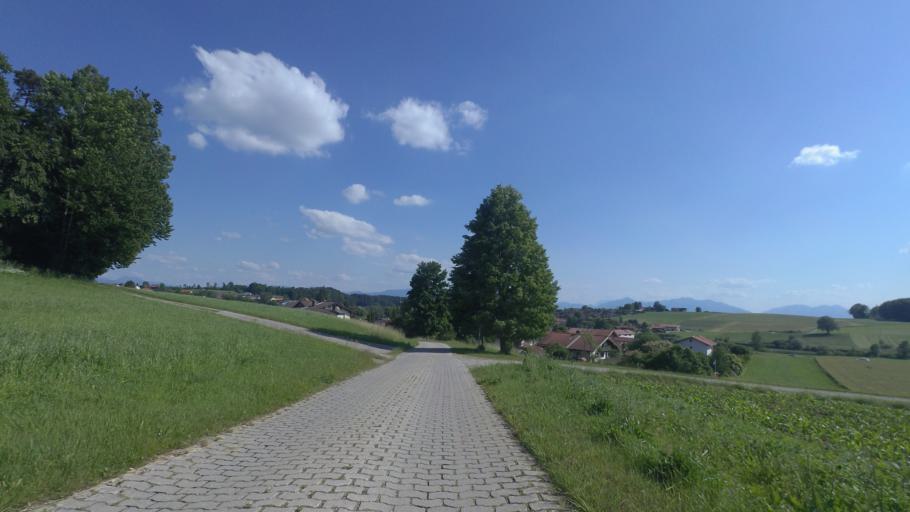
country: DE
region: Bavaria
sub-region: Upper Bavaria
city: Seeon-Seebruck
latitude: 47.9651
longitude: 12.4992
